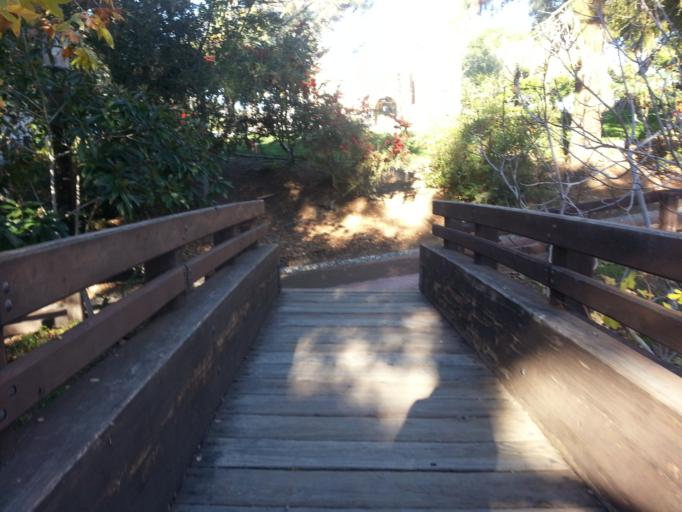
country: US
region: California
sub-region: San Luis Obispo County
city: San Luis Obispo
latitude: 35.2797
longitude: -120.6645
